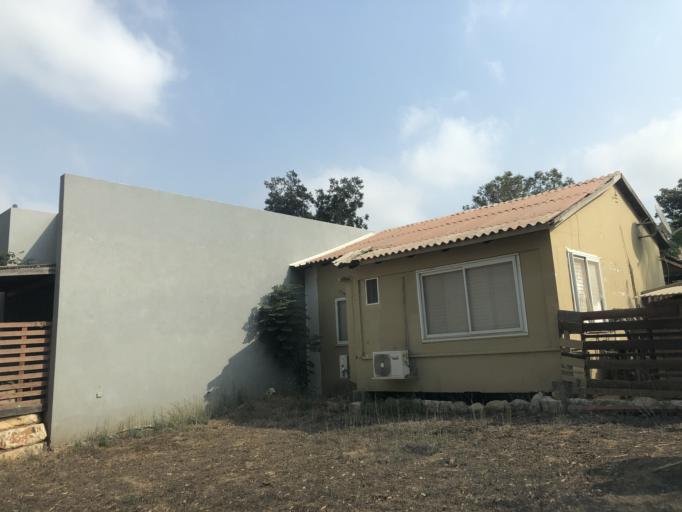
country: IL
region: Central District
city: Rosh Ha'Ayin
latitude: 32.0844
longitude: 34.9388
